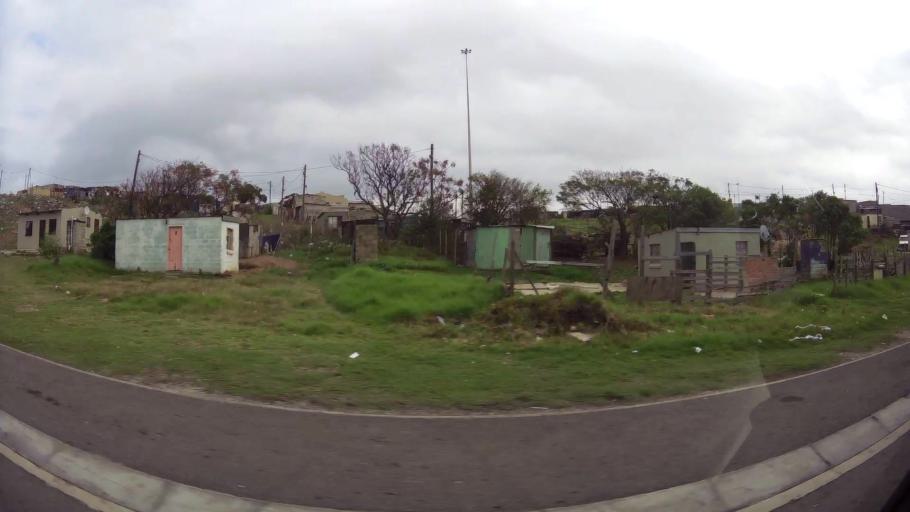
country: ZA
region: Eastern Cape
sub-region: Nelson Mandela Bay Metropolitan Municipality
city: Port Elizabeth
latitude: -33.9117
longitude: 25.5392
